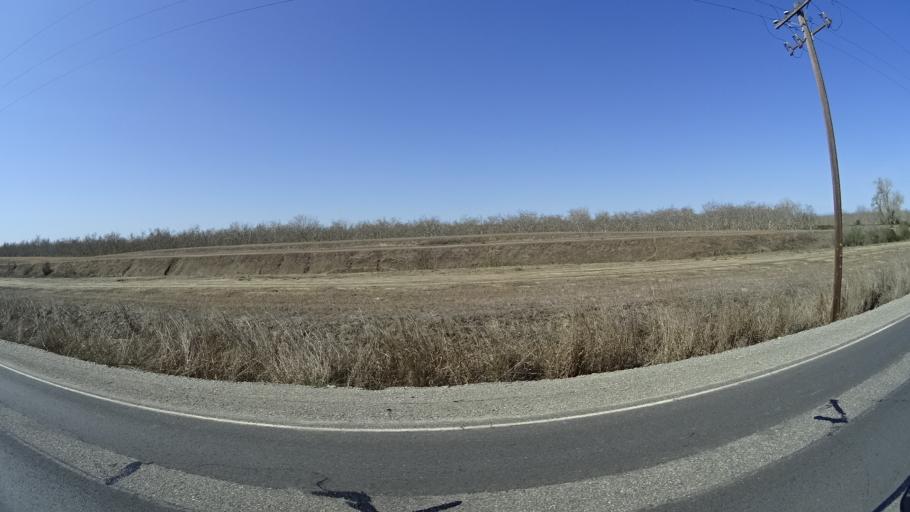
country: US
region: California
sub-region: Glenn County
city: Hamilton City
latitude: 39.7549
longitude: -122.0243
